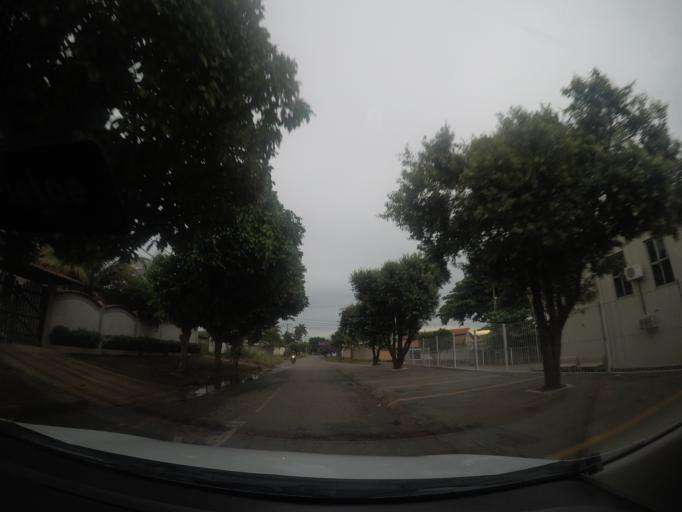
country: BR
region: Goias
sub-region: Goiania
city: Goiania
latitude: -16.6365
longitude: -49.2414
